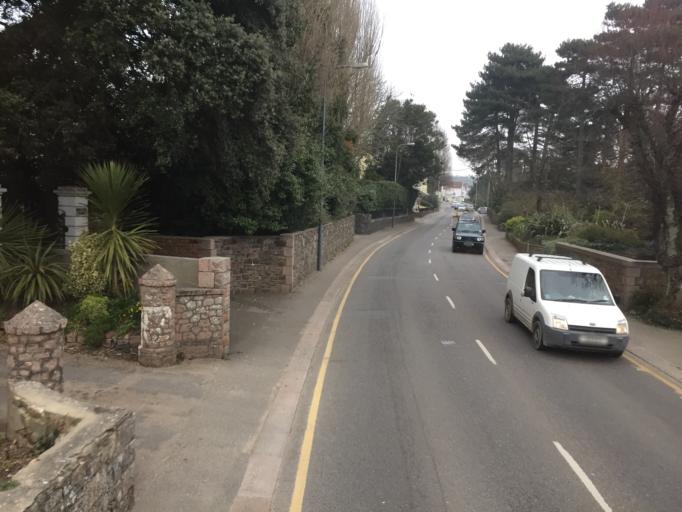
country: JE
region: St Helier
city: Saint Helier
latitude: 49.1986
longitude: -2.1426
